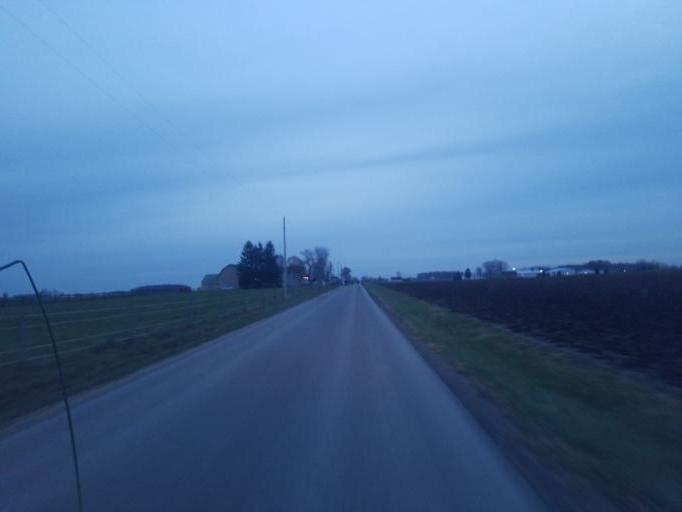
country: US
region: Indiana
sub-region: Adams County
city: Berne
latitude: 40.7271
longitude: -84.8984
